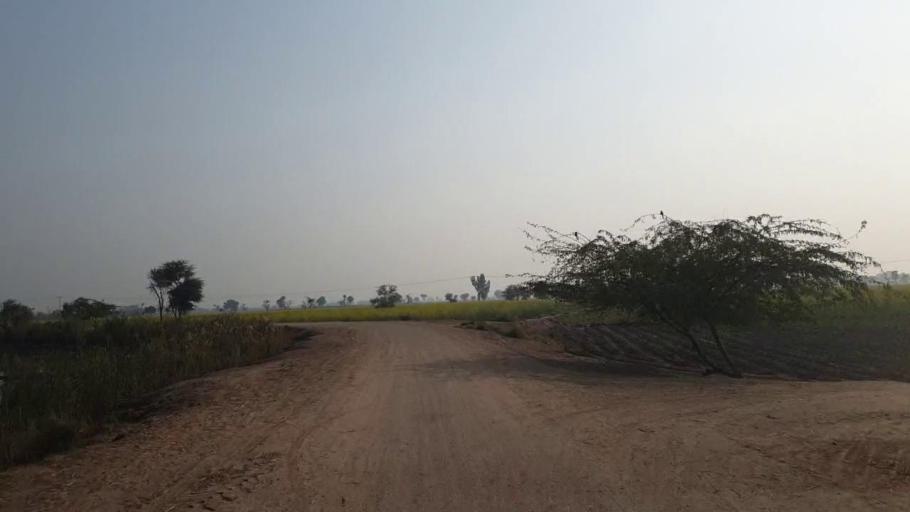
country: PK
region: Sindh
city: Shahdadpur
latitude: 25.9614
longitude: 68.5243
